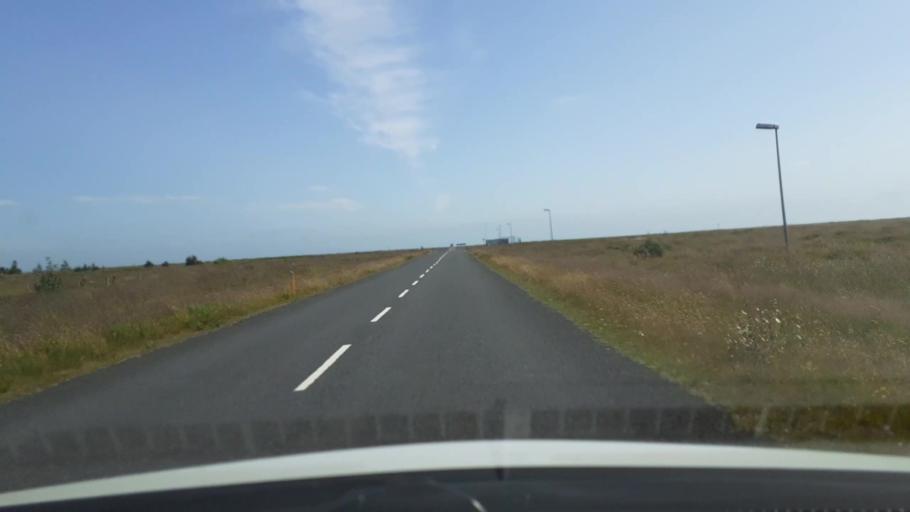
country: IS
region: South
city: Selfoss
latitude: 63.8933
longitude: -21.0810
